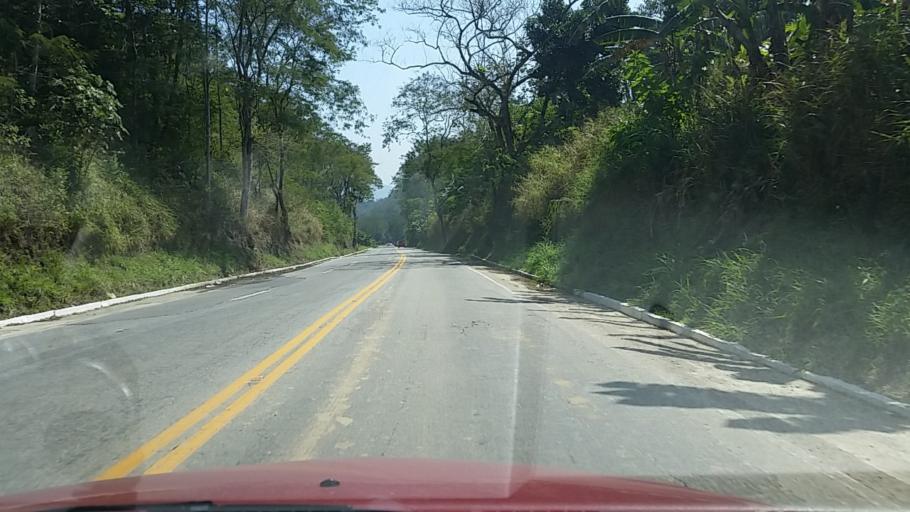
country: BR
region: Sao Paulo
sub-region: Miracatu
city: Miracatu
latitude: -24.3406
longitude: -47.4989
